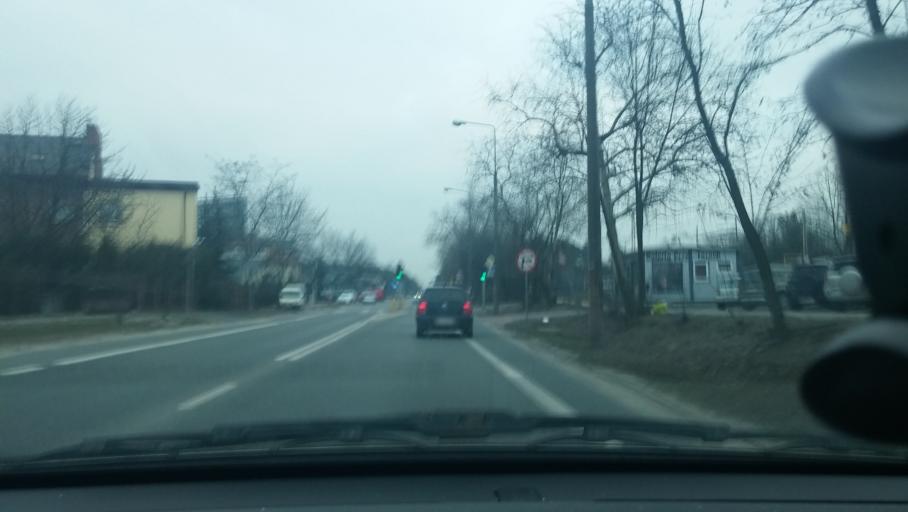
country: PL
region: Masovian Voivodeship
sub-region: Warszawa
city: Wawer
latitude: 52.2037
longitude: 21.1698
